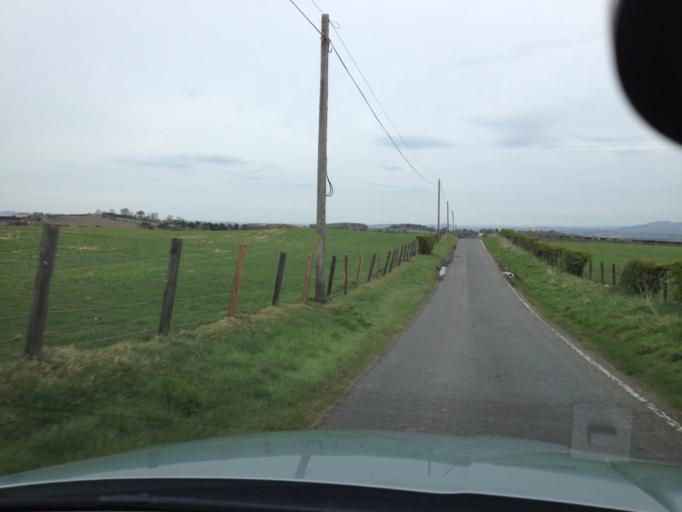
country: GB
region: Scotland
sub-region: West Lothian
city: Linlithgow
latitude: 55.9299
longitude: -3.5738
